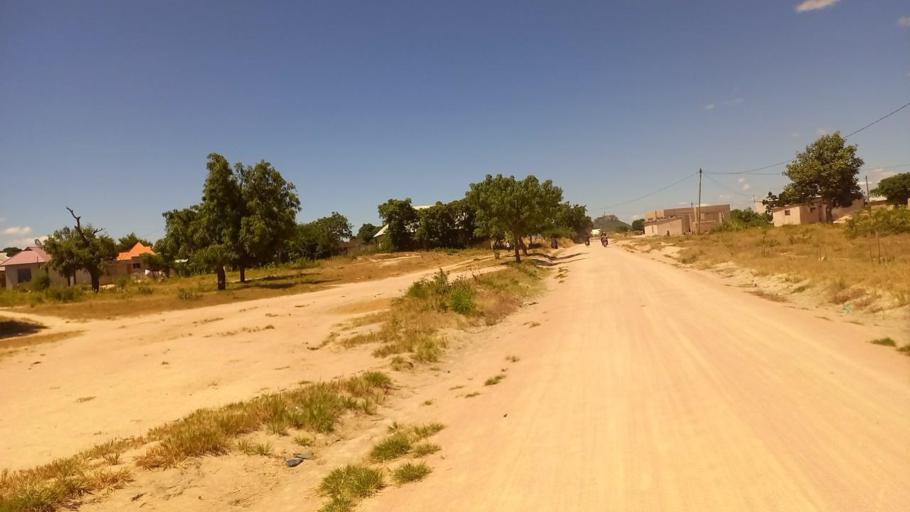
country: TZ
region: Dodoma
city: Dodoma
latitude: -6.1309
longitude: 35.7323
